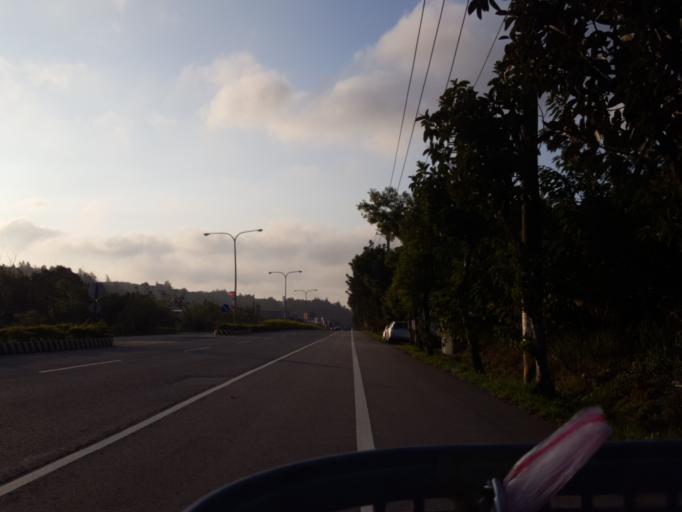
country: TW
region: Taiwan
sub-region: Hsinchu
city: Zhubei
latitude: 24.8811
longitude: 121.0342
